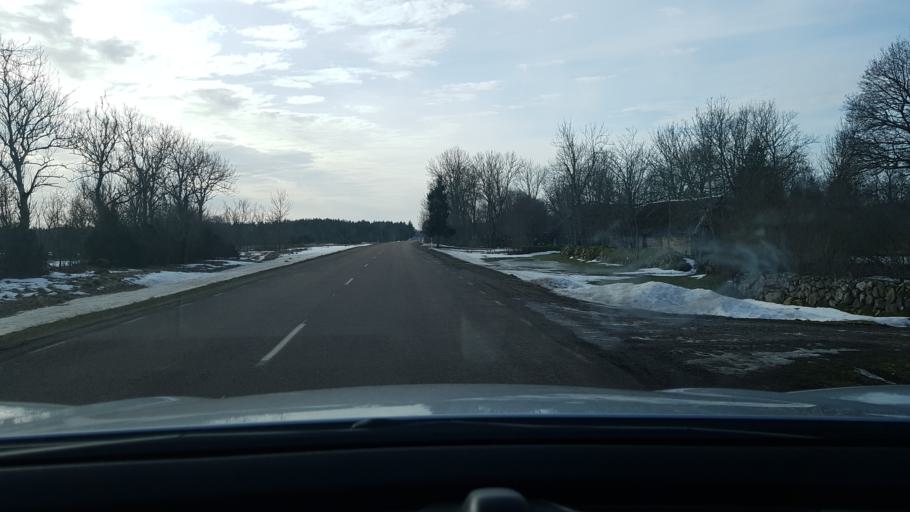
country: EE
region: Saare
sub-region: Kuressaare linn
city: Kuressaare
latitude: 58.3280
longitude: 22.5576
